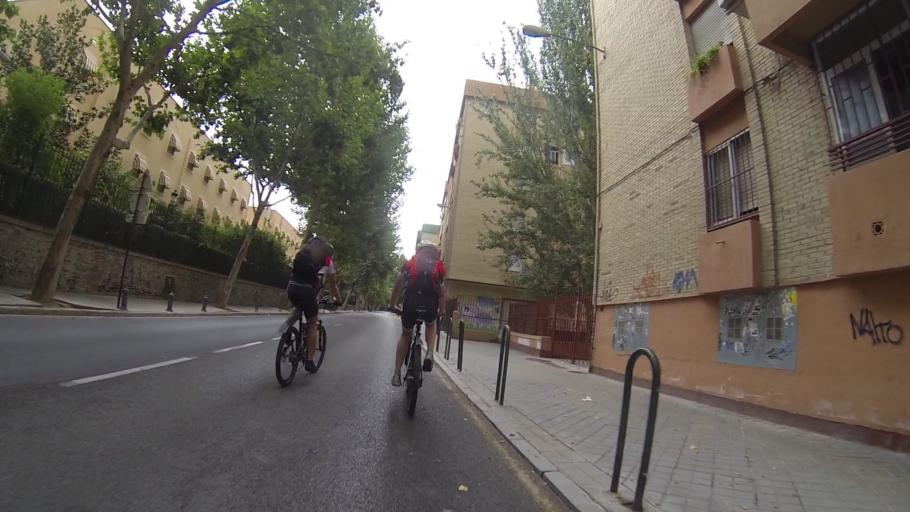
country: ES
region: Andalusia
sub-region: Provincia de Granada
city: Granada
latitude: 37.1909
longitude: -3.6143
